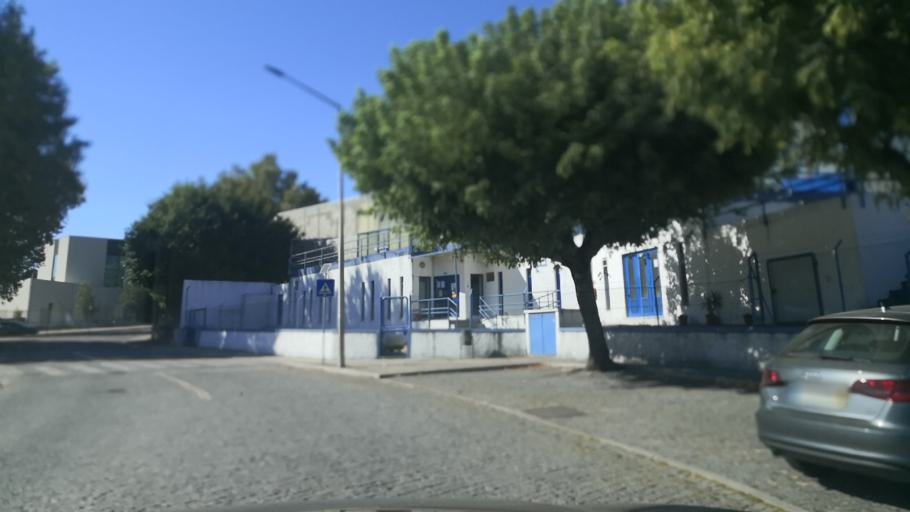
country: PT
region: Porto
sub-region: Santo Tirso
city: Santo Tirso
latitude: 41.3408
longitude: -8.4826
